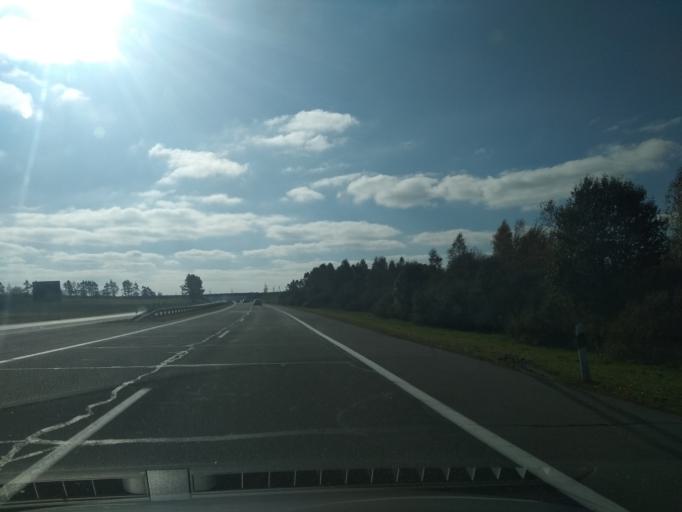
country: BY
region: Brest
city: Baranovichi
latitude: 53.1162
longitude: 25.8956
